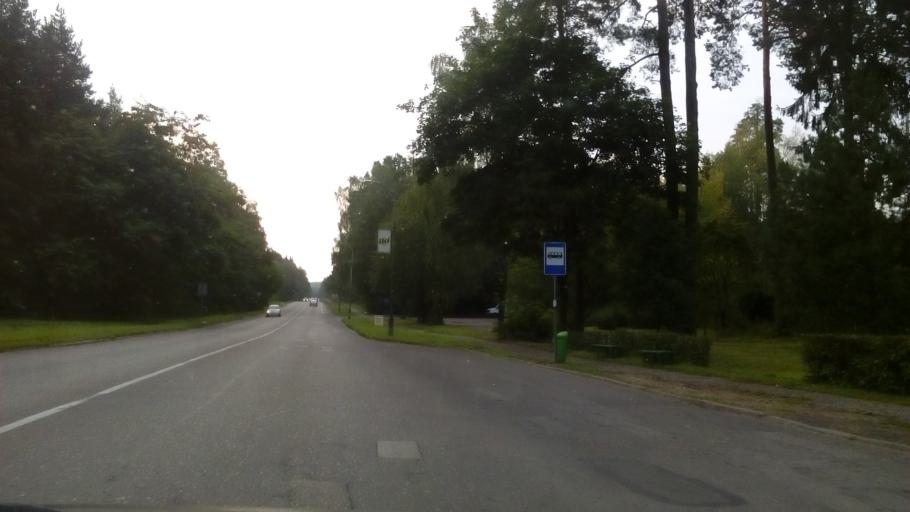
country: LT
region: Alytaus apskritis
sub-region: Alytus
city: Alytus
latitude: 54.3793
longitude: 24.0635
